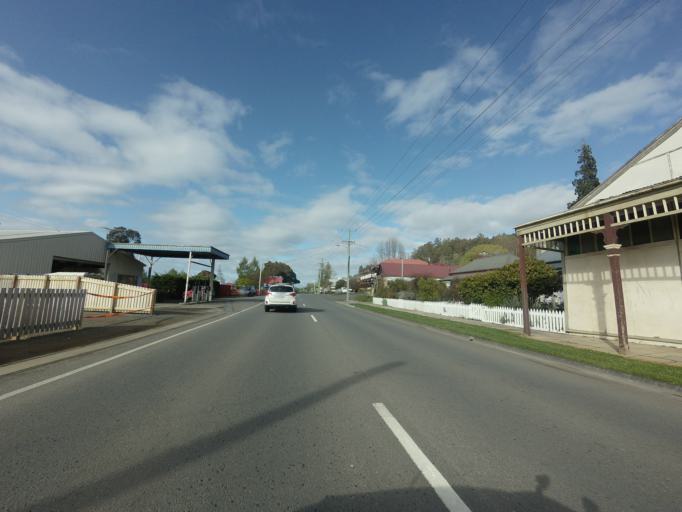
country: AU
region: Tasmania
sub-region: Huon Valley
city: Franklin
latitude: -43.0922
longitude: 147.0088
